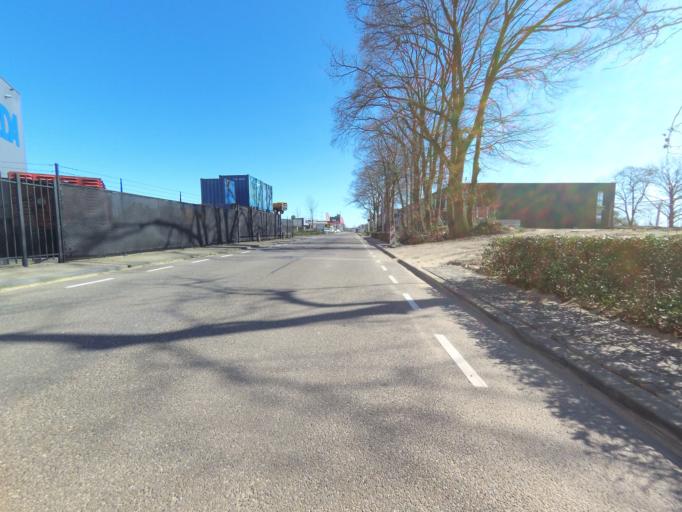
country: NL
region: Utrecht
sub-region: Gemeente Woudenberg
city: Woudenberg
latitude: 52.0844
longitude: 5.4474
